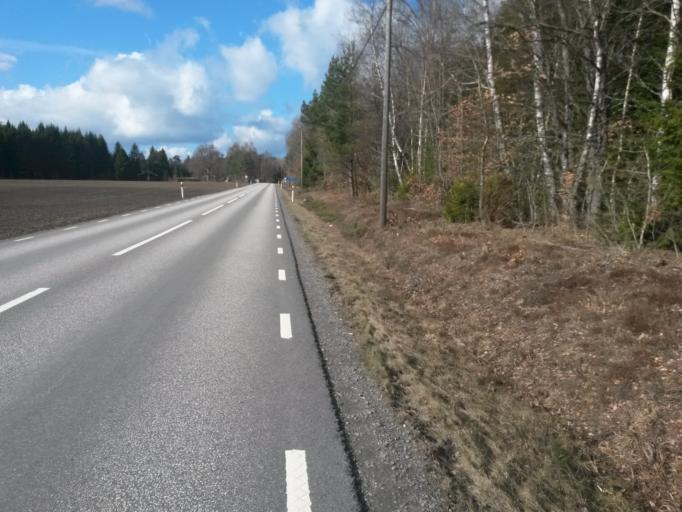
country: SE
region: Vaestra Goetaland
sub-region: Vargarda Kommun
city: Jonstorp
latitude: 58.0627
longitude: 12.6886
